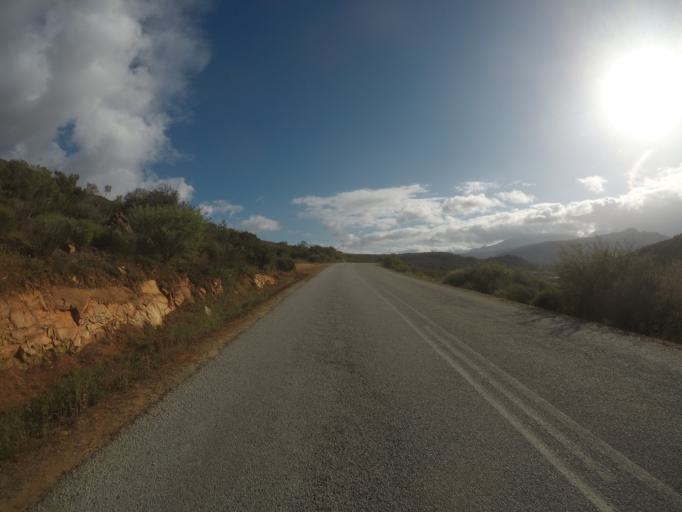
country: ZA
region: Western Cape
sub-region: West Coast District Municipality
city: Clanwilliam
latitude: -32.4357
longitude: 18.9461
